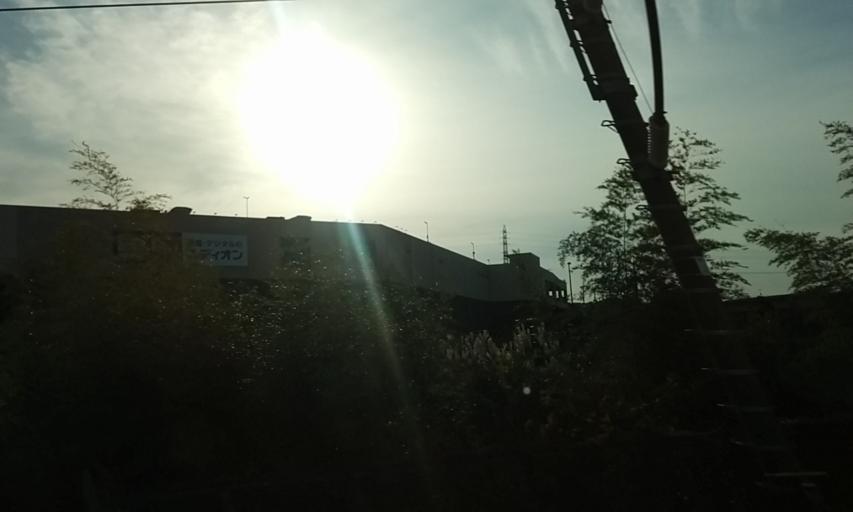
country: JP
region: Shiga Prefecture
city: Kusatsu
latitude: 34.9742
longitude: 135.9318
